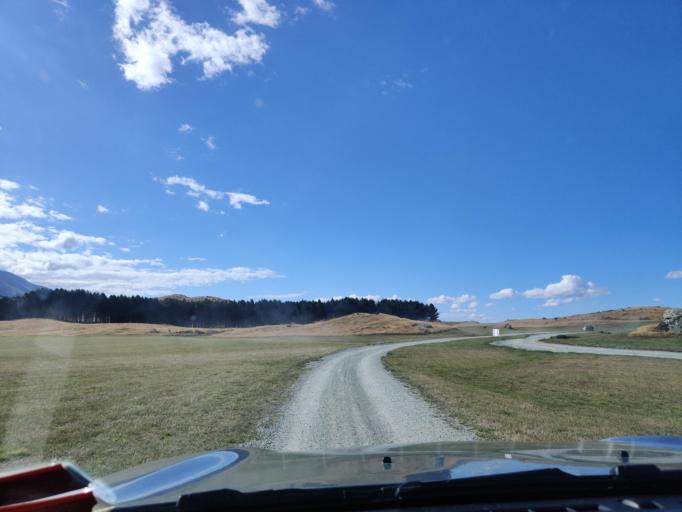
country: NZ
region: Canterbury
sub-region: Timaru District
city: Pleasant Point
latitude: -44.1368
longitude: 170.1177
